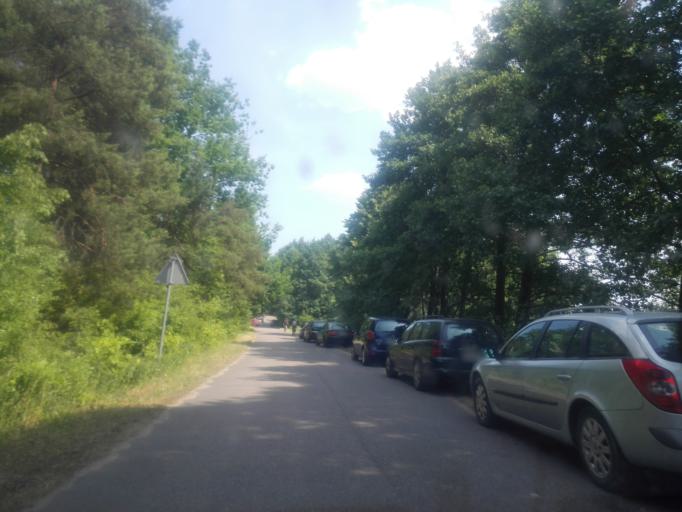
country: PL
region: Podlasie
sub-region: Suwalki
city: Suwalki
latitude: 54.0183
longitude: 23.0213
